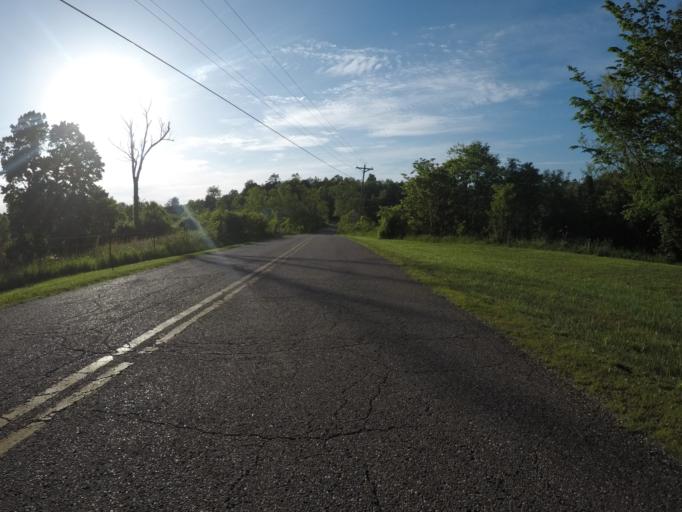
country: US
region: West Virginia
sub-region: Cabell County
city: Huntington
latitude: 38.5316
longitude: -82.4246
